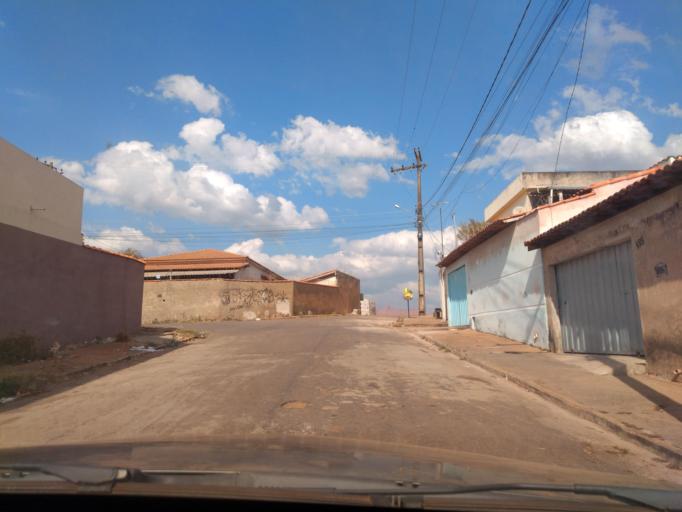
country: BR
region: Minas Gerais
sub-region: Tres Coracoes
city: Tres Coracoes
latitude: -21.6857
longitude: -45.2351
